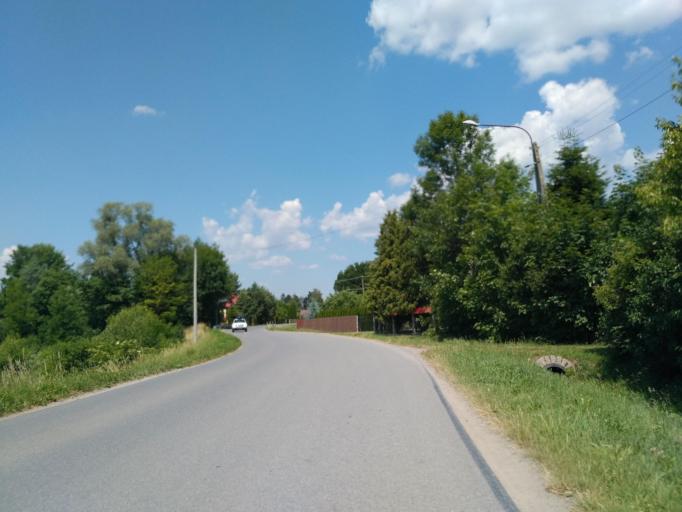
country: PL
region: Subcarpathian Voivodeship
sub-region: Powiat sanocki
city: Niebieszczany
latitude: 49.5289
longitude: 22.1280
